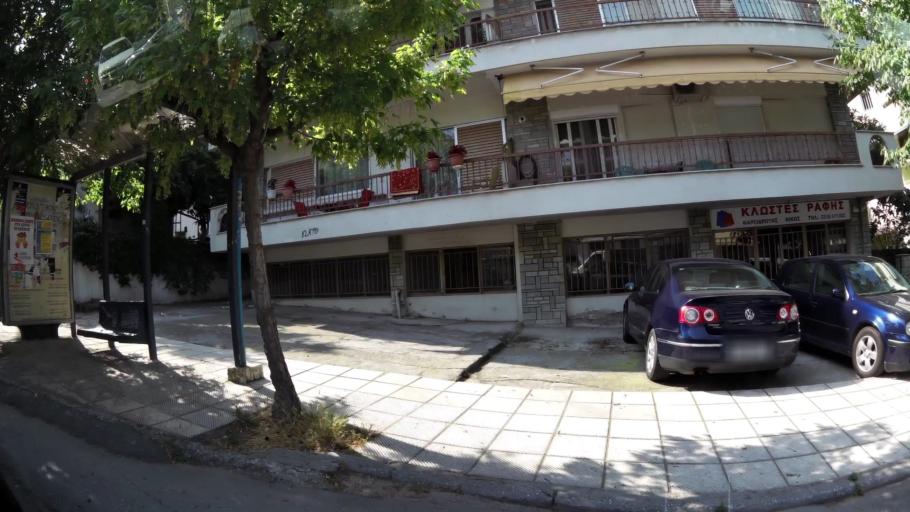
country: GR
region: Central Macedonia
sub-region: Nomos Thessalonikis
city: Sykies
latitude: 40.6512
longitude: 22.9510
